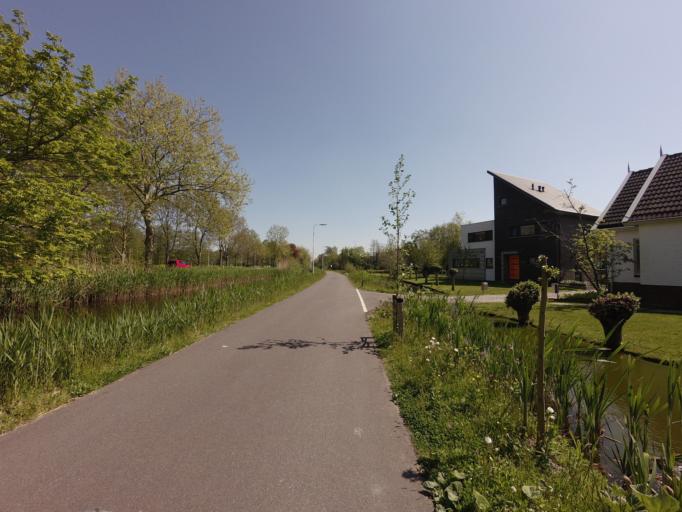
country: NL
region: South Holland
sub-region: Gemeente Gouda
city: Gouda
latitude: 52.0173
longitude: 4.7339
